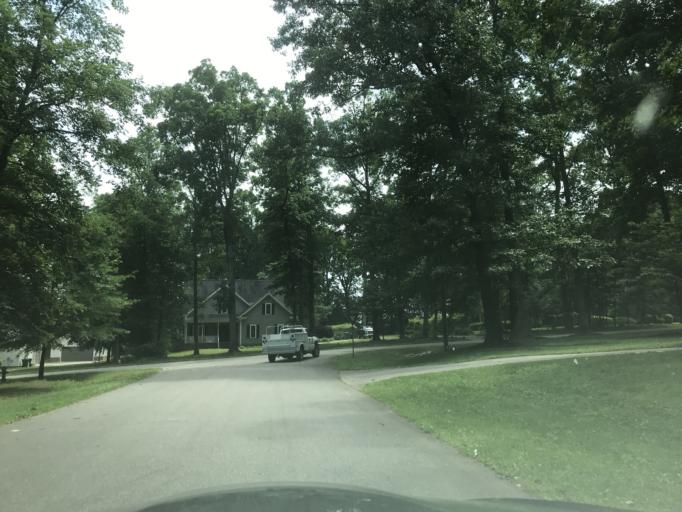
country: US
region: North Carolina
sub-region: Wake County
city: Raleigh
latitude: 35.8589
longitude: -78.5842
